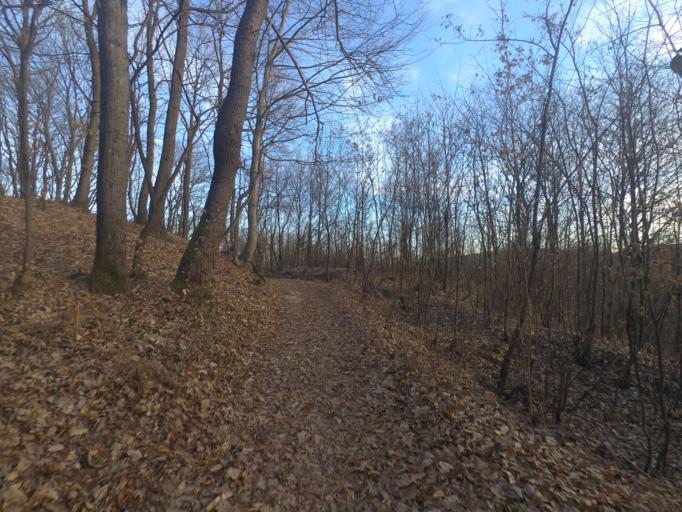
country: HR
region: Karlovacka
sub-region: Grad Karlovac
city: Karlovac
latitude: 45.4750
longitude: 15.5306
